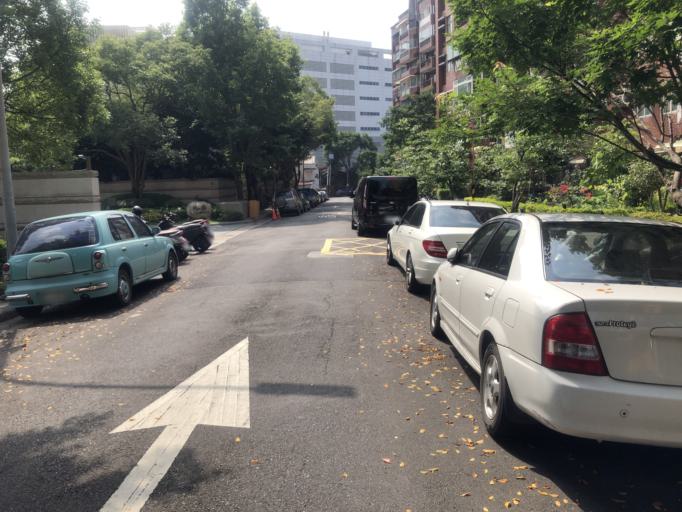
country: TW
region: Taipei
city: Taipei
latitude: 25.0839
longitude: 121.5389
